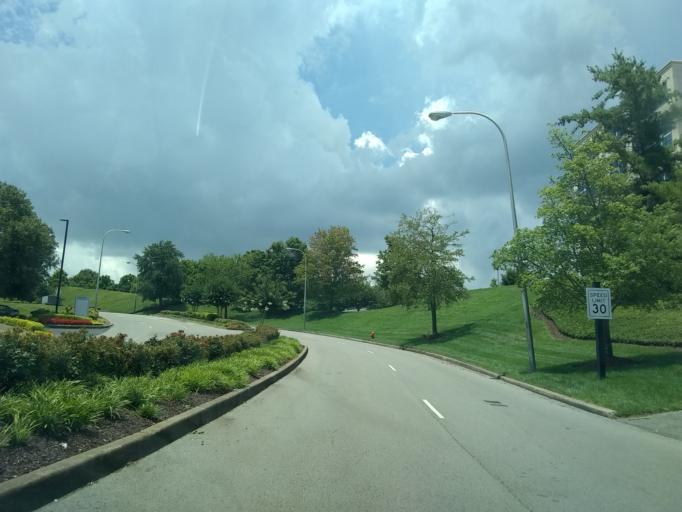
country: US
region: Tennessee
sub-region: Davidson County
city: Nashville
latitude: 36.1488
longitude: -86.6842
